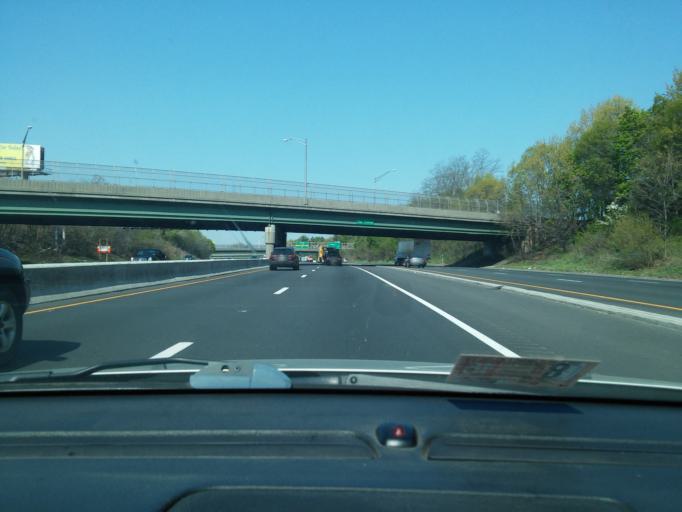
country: US
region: New Jersey
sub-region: Union County
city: Hillside
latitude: 40.7165
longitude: -74.2113
